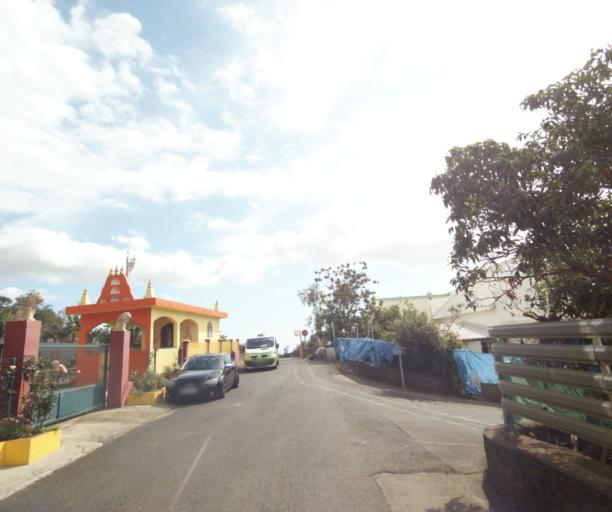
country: RE
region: Reunion
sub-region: Reunion
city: Saint-Paul
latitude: -21.0304
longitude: 55.2858
